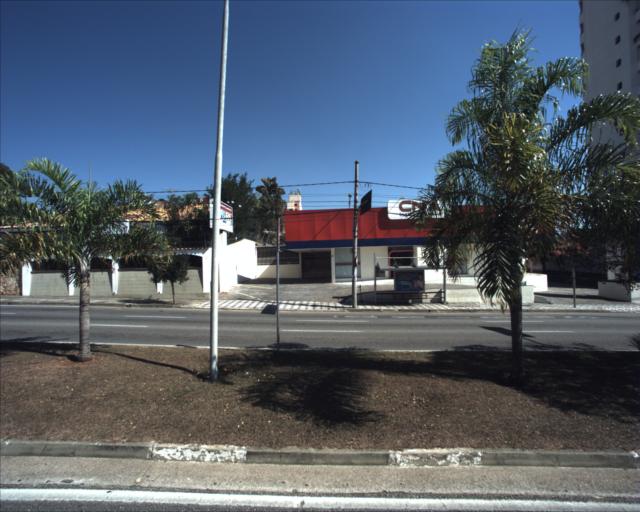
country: BR
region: Sao Paulo
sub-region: Sorocaba
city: Sorocaba
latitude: -23.5020
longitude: -47.4683
